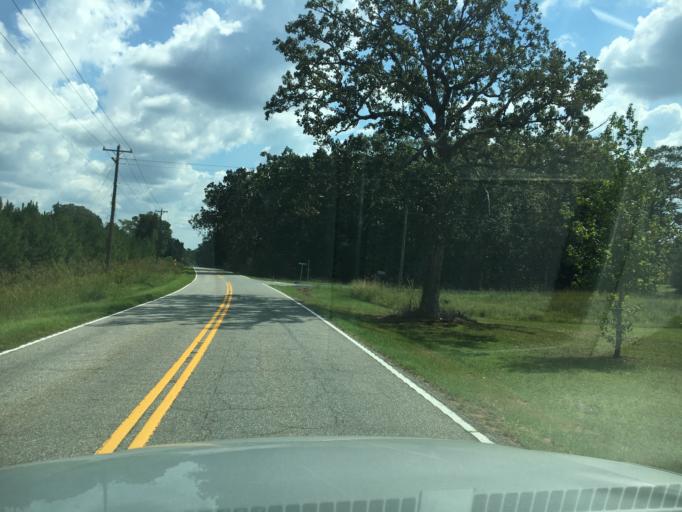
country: US
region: South Carolina
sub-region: Greenwood County
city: Greenwood
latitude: 34.0651
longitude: -82.1456
